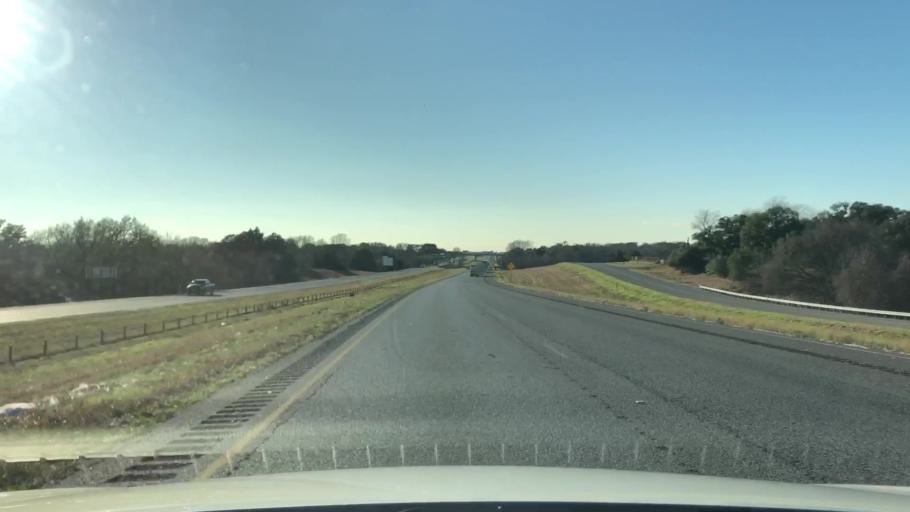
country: US
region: Texas
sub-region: Fayette County
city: Schulenburg
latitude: 29.6911
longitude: -96.9188
